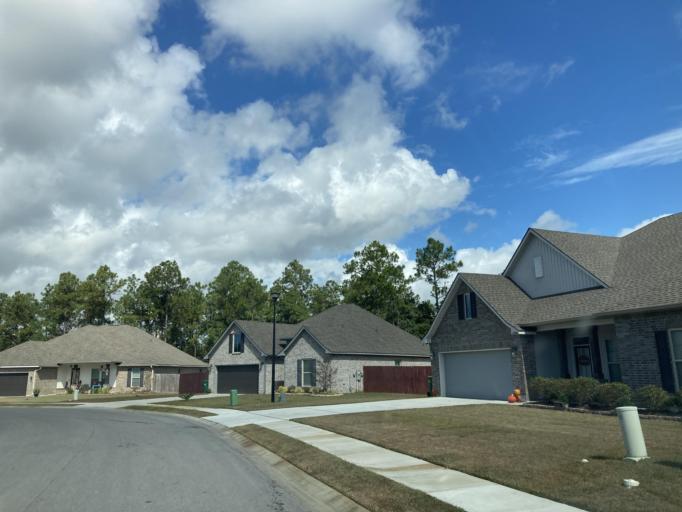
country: US
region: Mississippi
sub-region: Jackson County
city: Gulf Hills
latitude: 30.4530
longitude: -88.8233
